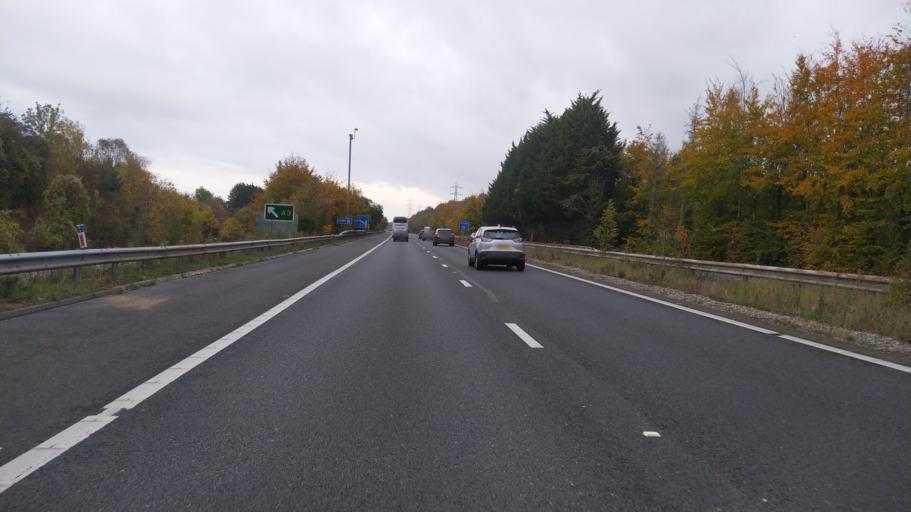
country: GB
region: England
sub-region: Hampshire
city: Cowplain
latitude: 50.9218
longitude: -0.9980
